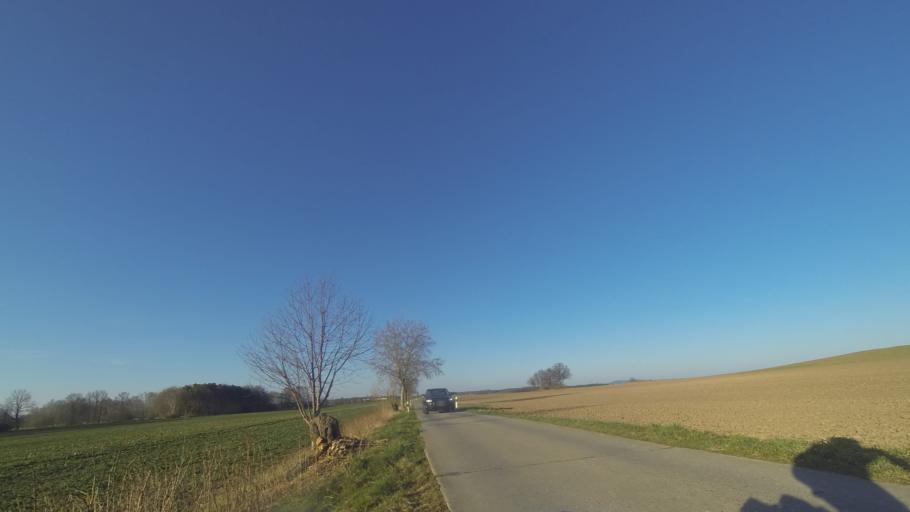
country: DE
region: Saxony
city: Radeburg
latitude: 51.1694
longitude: 13.7707
